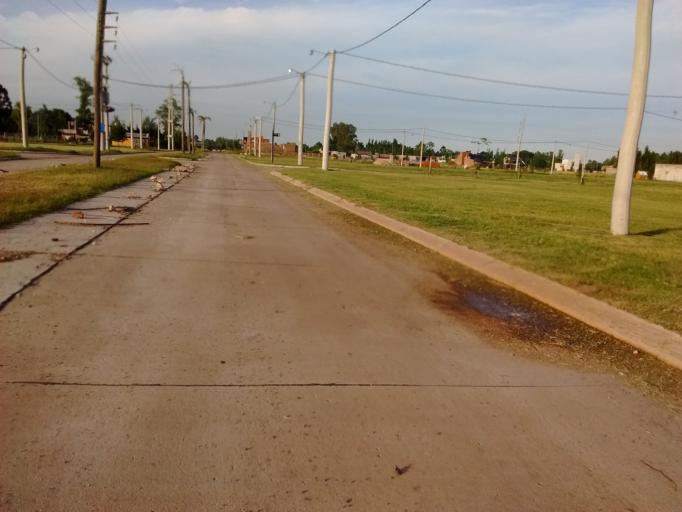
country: AR
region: Santa Fe
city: Roldan
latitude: -32.9253
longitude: -60.8737
